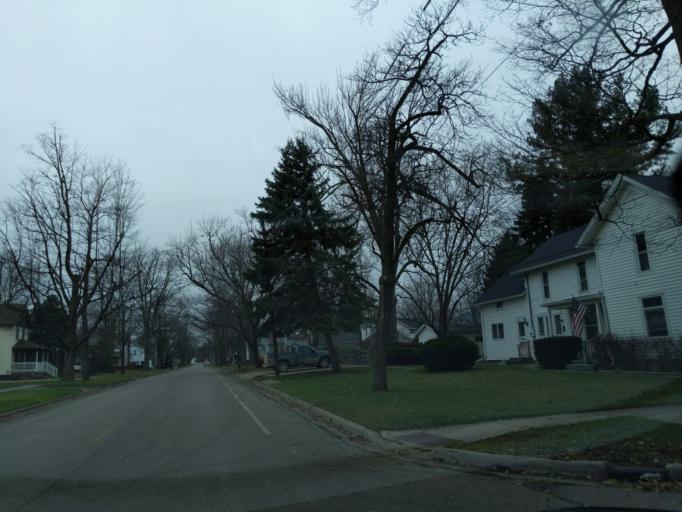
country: US
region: Michigan
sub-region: Clinton County
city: Saint Johns
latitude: 42.9972
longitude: -84.5572
